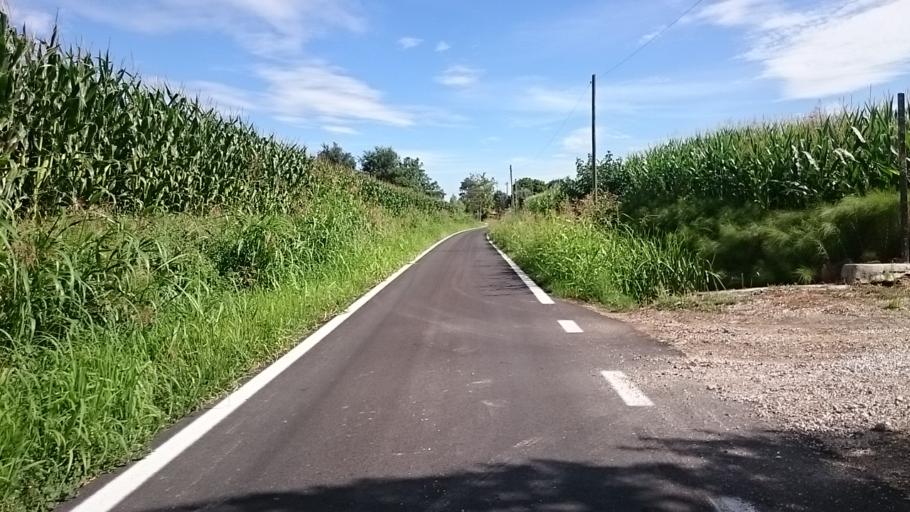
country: IT
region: Veneto
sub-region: Provincia di Padova
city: Albignasego
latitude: 45.3322
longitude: 11.8904
